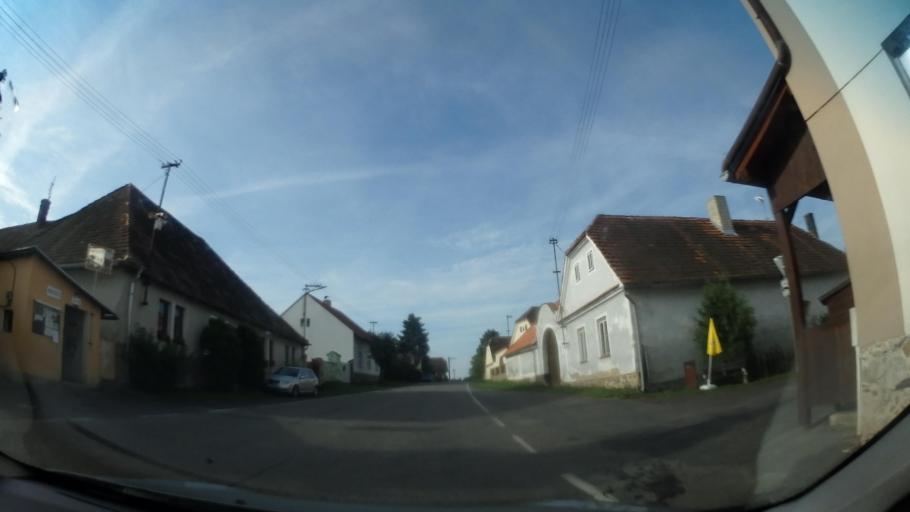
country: CZ
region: Jihocesky
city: Cimelice
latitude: 49.4773
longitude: 14.1529
